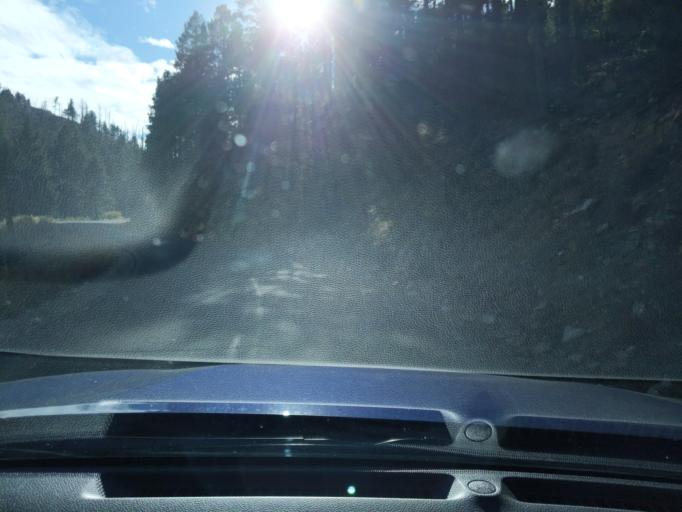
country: US
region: Arizona
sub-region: Pima County
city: Catalina
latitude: 32.4473
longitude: -110.7866
